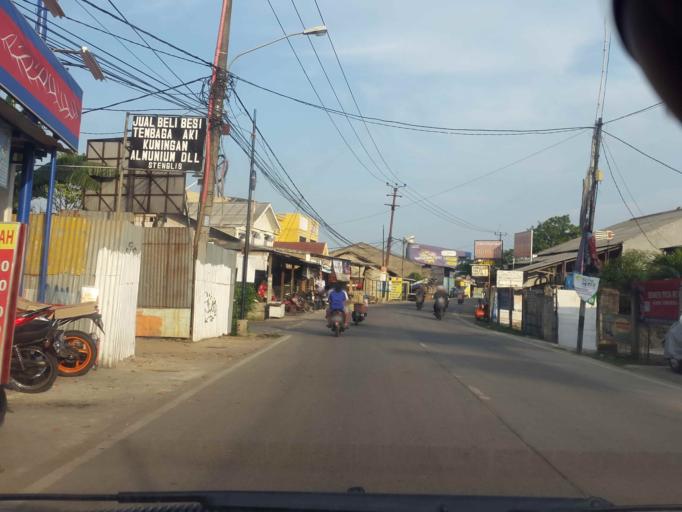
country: ID
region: West Java
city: Ciputat
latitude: -6.2599
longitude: 106.7084
